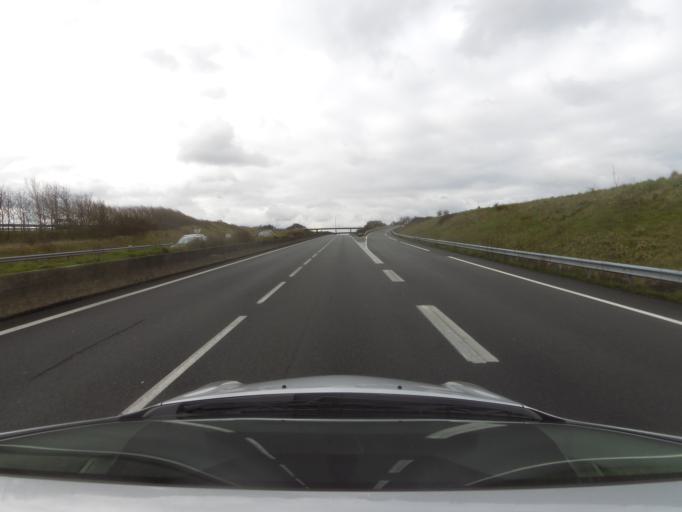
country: FR
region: Nord-Pas-de-Calais
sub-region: Departement du Pas-de-Calais
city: Wimille
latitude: 50.7738
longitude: 1.6518
